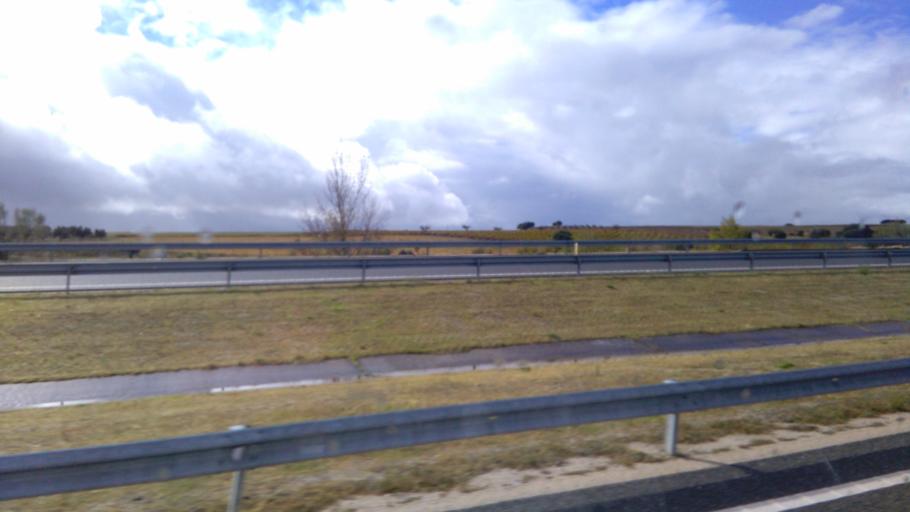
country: ES
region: Madrid
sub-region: Provincia de Madrid
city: El Alamo
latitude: 40.2597
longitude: -3.9871
